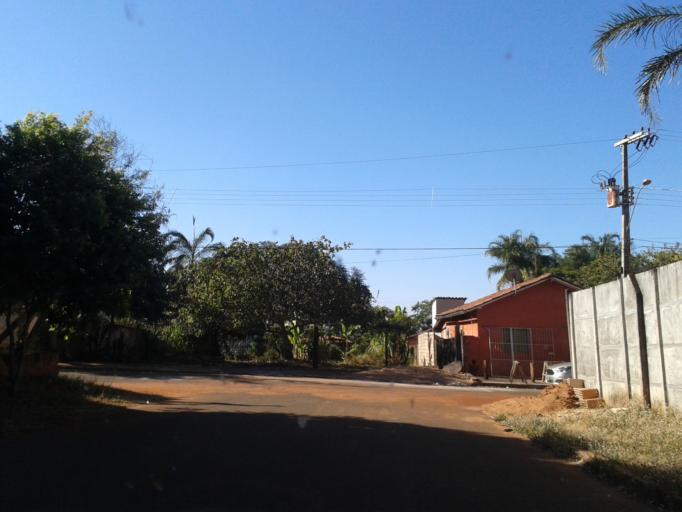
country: BR
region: Minas Gerais
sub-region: Santa Vitoria
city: Santa Vitoria
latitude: -18.9322
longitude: -49.8393
